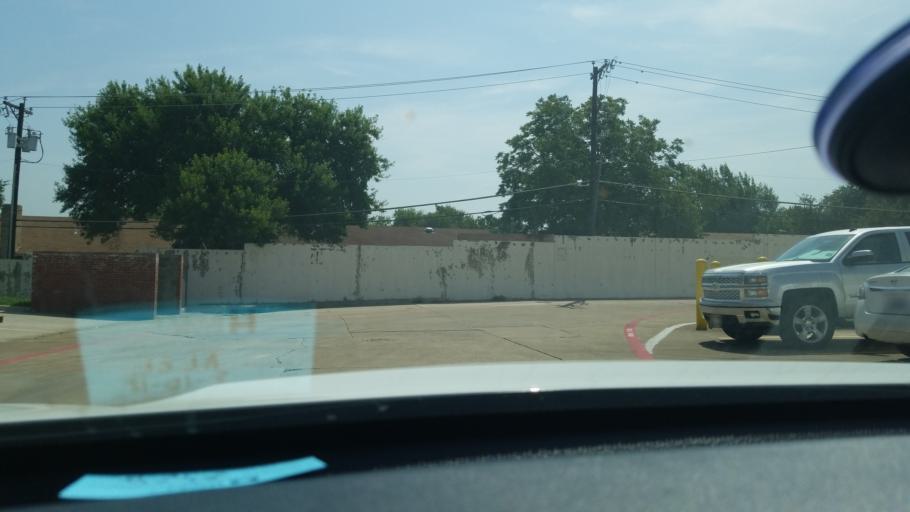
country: US
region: Texas
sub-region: Dallas County
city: Carrollton
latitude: 32.9916
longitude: -96.8887
